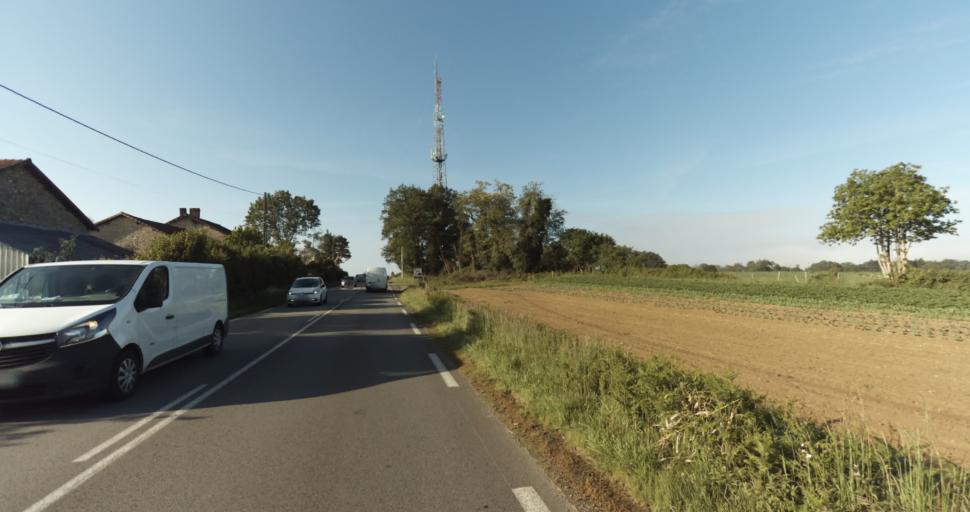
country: FR
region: Limousin
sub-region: Departement de la Haute-Vienne
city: Condat-sur-Vienne
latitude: 45.7793
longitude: 1.2889
